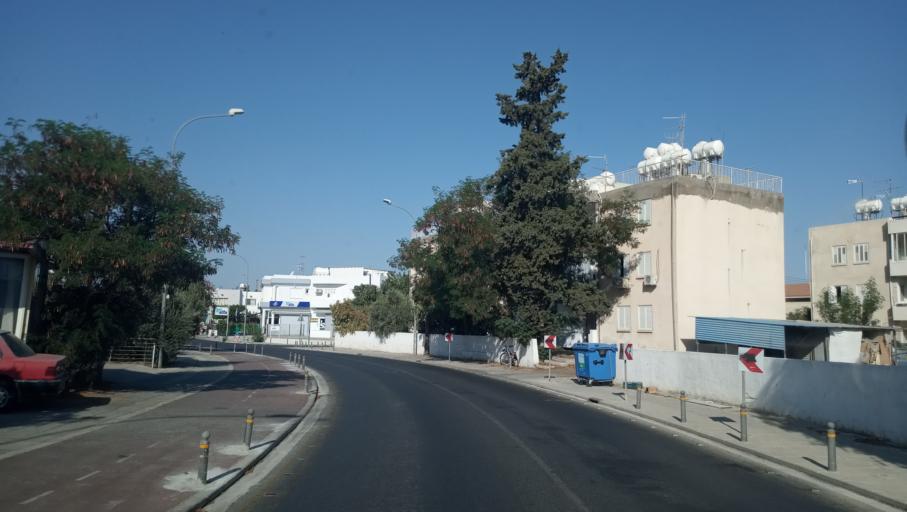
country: CY
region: Lefkosia
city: Nicosia
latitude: 35.1507
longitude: 33.3976
